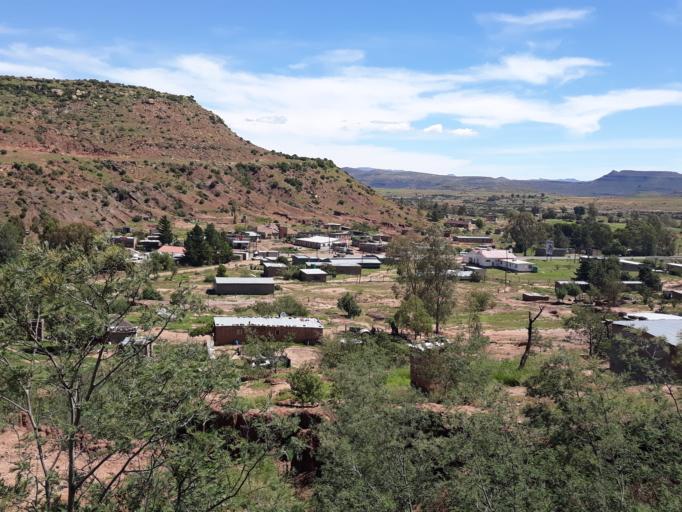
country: LS
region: Quthing
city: Quthing
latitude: -30.3393
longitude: 27.5416
